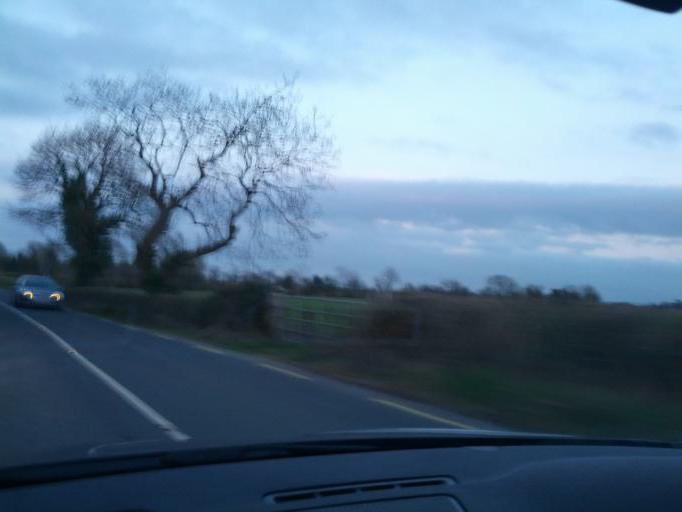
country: IE
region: Leinster
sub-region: Uibh Fhaili
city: Banagher
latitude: 53.0925
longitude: -8.0375
